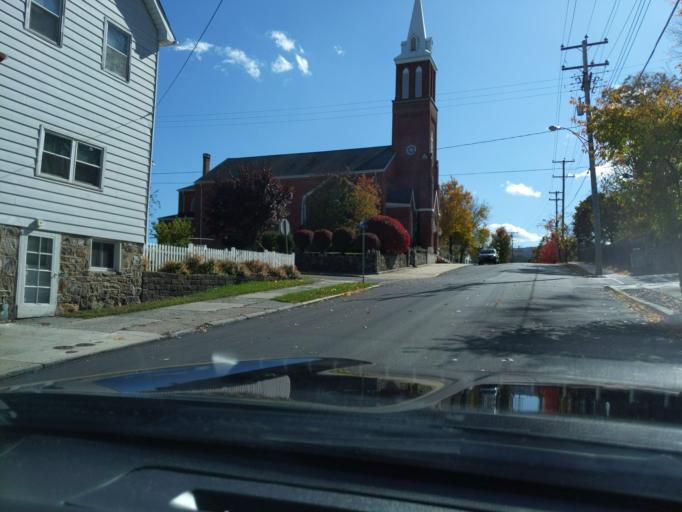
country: US
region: Pennsylvania
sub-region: Blair County
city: Hollidaysburg
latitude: 40.4318
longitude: -78.3966
